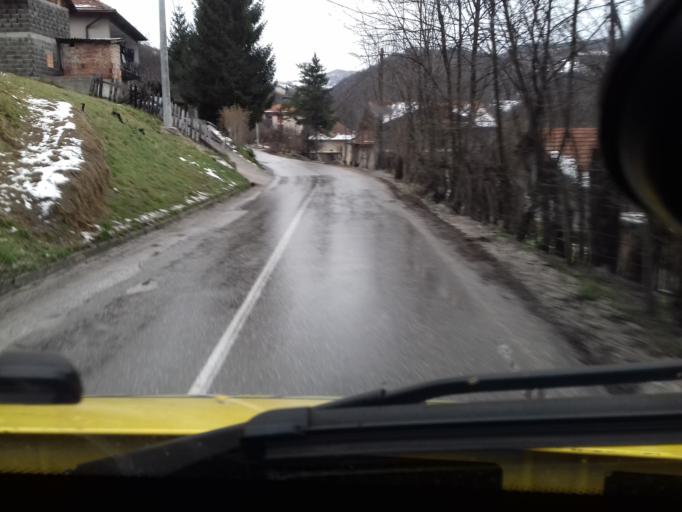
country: BA
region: Federation of Bosnia and Herzegovina
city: Lokvine
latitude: 44.1999
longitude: 17.8688
